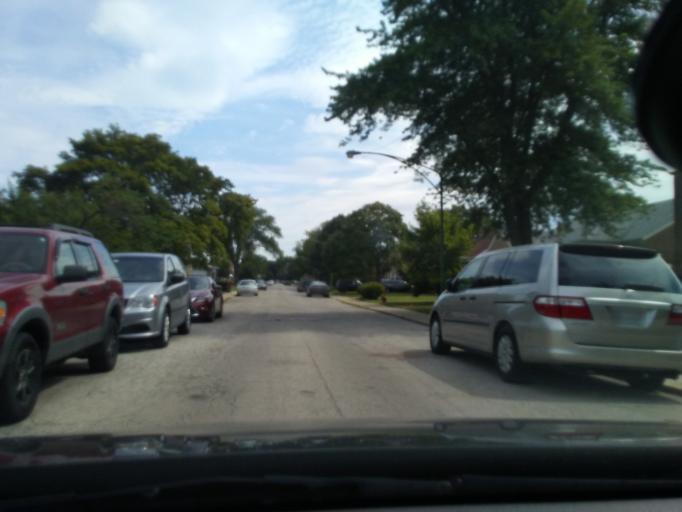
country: US
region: Illinois
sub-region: Cook County
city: Harwood Heights
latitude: 41.9751
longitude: -87.7855
